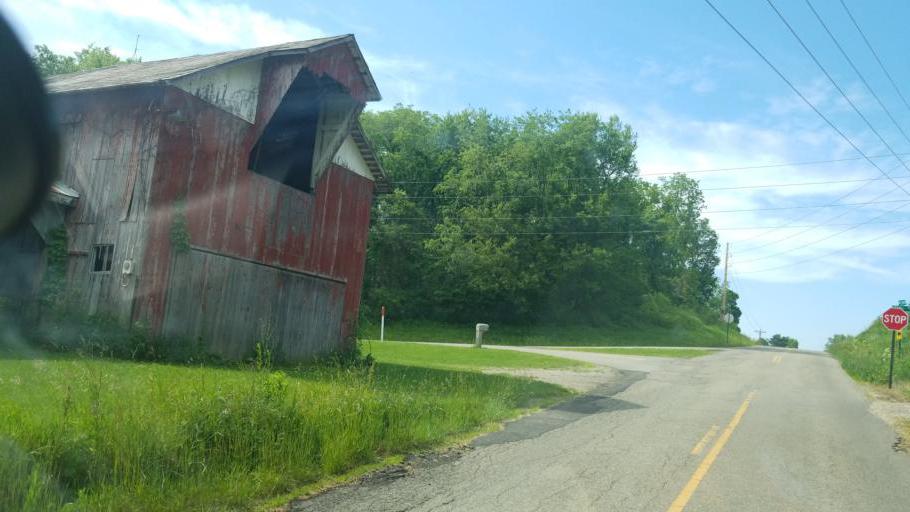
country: US
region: Ohio
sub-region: Knox County
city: Gambier
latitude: 40.3361
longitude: -82.3584
